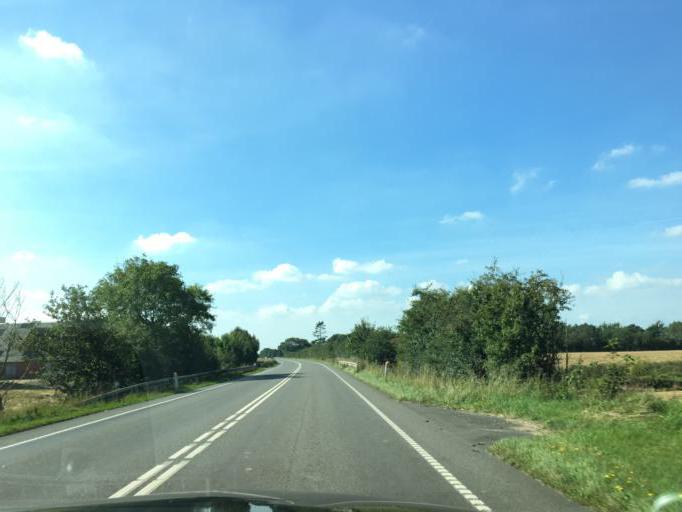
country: DK
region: South Denmark
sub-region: Vejen Kommune
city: Vejen
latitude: 55.4730
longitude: 9.2039
